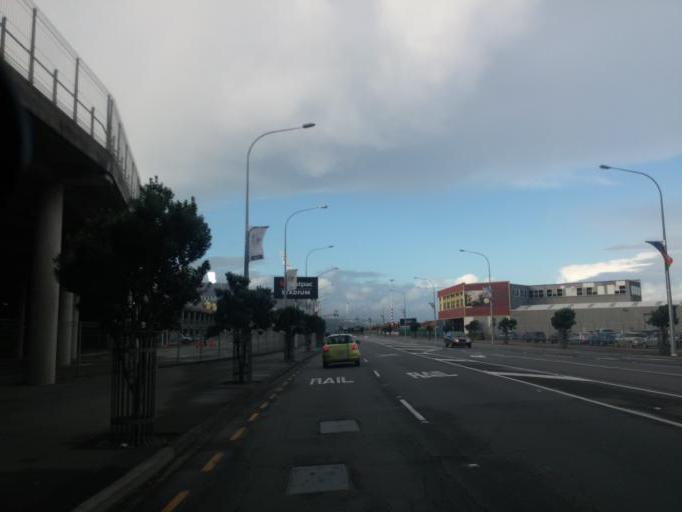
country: NZ
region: Wellington
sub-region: Wellington City
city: Wellington
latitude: -41.2764
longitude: 174.7839
